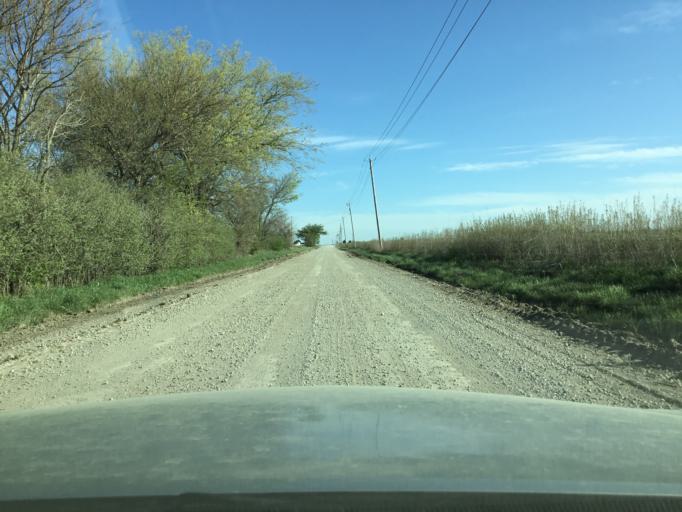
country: US
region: Kansas
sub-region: Neosho County
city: Chanute
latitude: 37.6569
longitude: -95.4892
